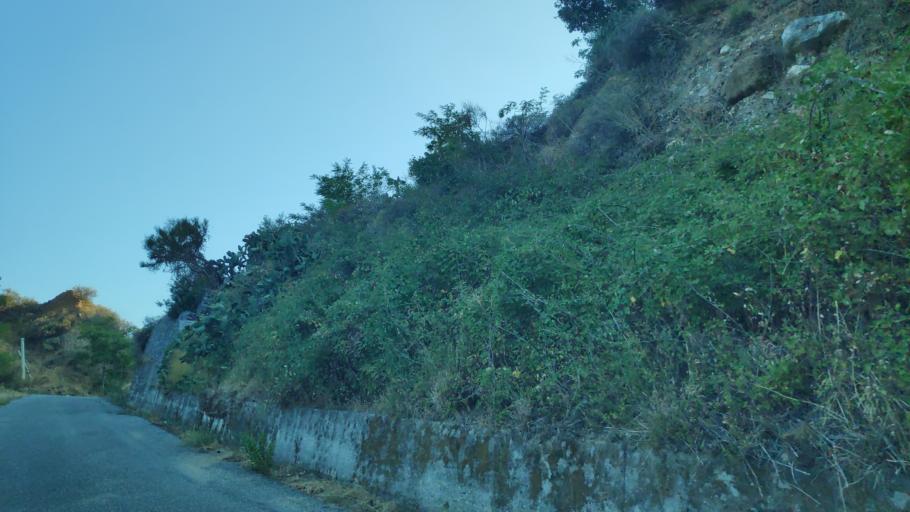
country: IT
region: Calabria
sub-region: Provincia di Reggio Calabria
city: Placanica
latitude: 38.4112
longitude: 16.4297
